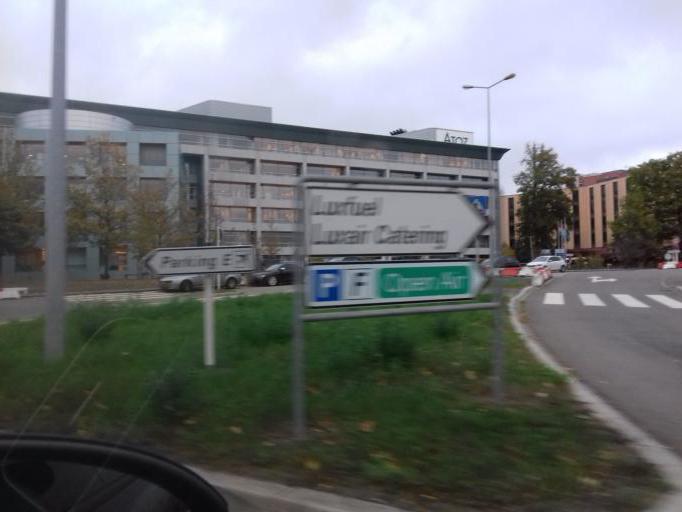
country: LU
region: Luxembourg
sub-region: Canton de Luxembourg
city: Sandweiler
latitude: 49.6368
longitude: 6.2167
